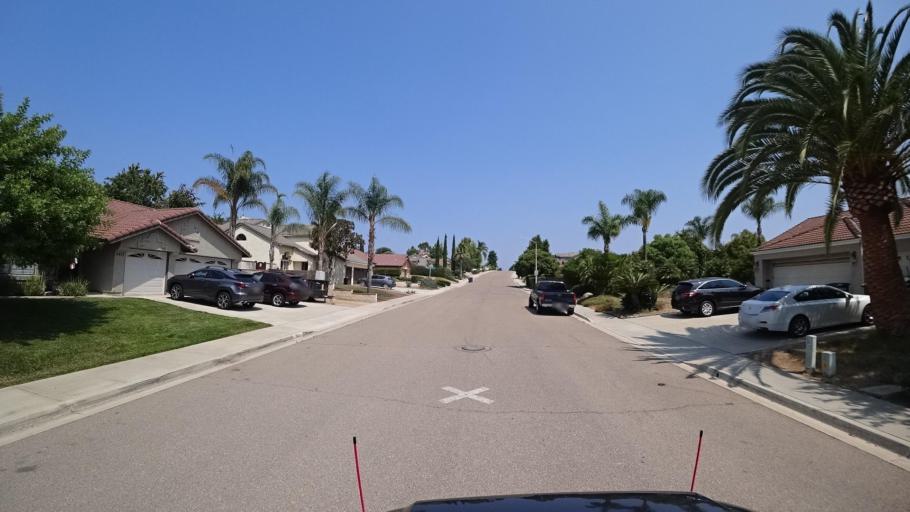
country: US
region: California
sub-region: San Diego County
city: Bonsall
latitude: 33.2919
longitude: -117.2273
